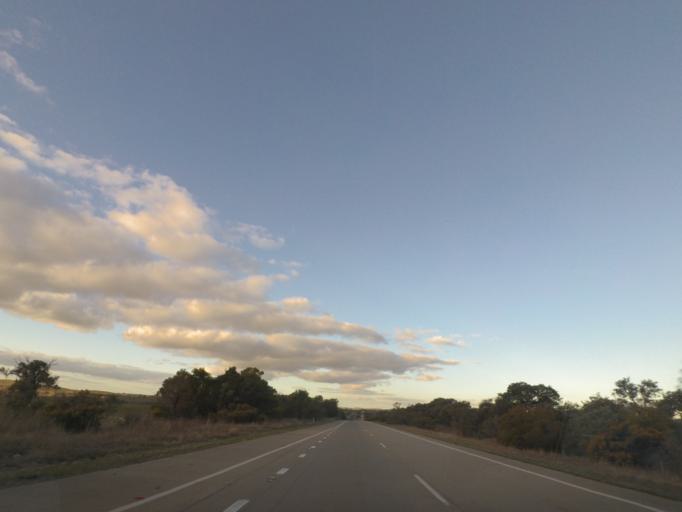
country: AU
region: New South Wales
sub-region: Yass Valley
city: Yass
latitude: -34.7733
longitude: 148.7387
